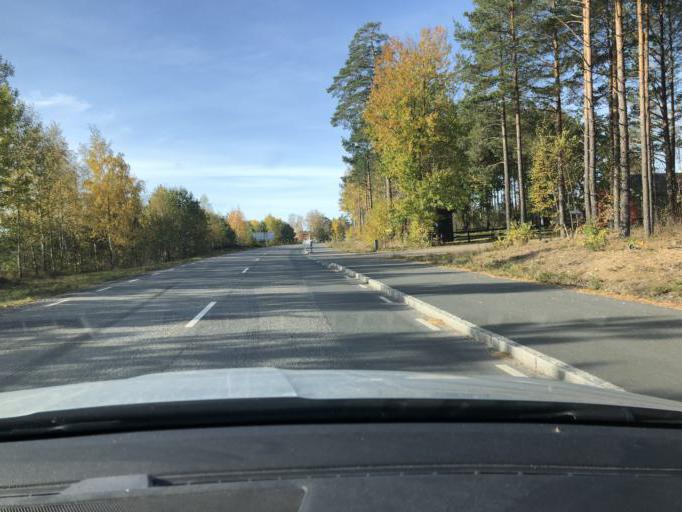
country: SE
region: Joenkoeping
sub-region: Jonkopings Kommun
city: Jonkoping
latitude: 57.7714
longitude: 14.0971
